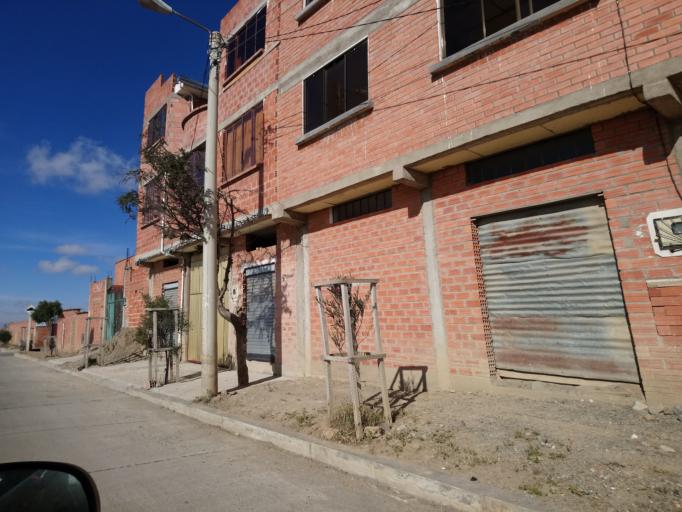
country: BO
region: La Paz
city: La Paz
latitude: -16.5088
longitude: -68.2053
